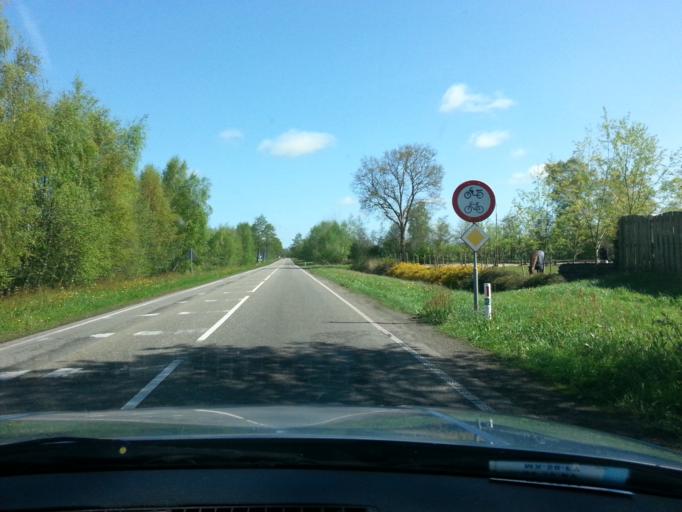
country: NL
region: Friesland
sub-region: Gemeente Achtkarspelen
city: Surhuisterveen
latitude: 53.1765
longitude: 6.1841
